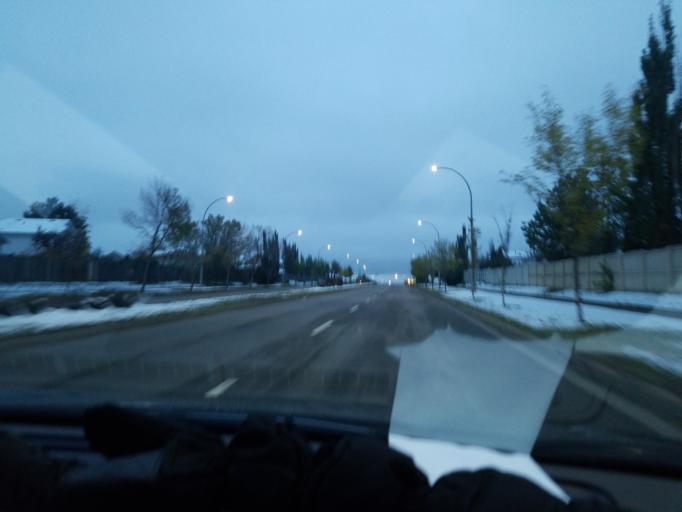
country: CA
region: Alberta
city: Edmonton
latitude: 53.6157
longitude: -113.4228
